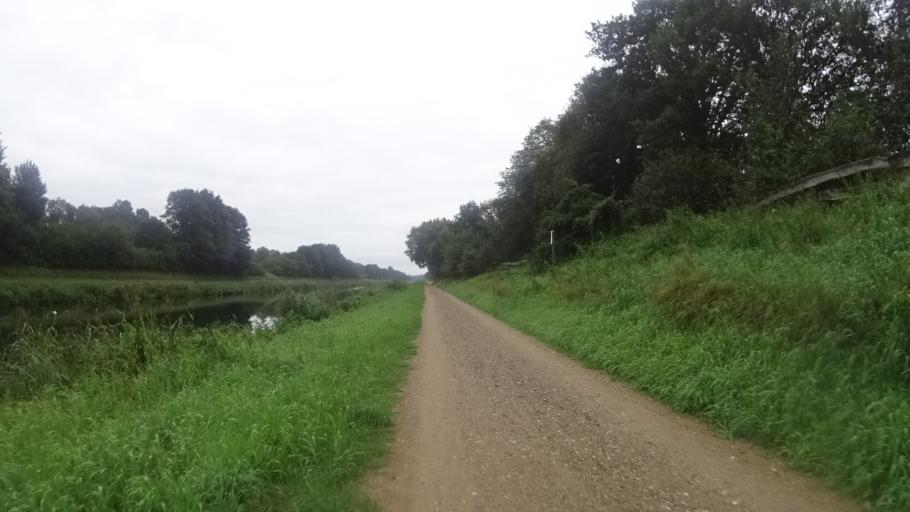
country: DE
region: Schleswig-Holstein
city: Grambek
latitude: 53.5657
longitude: 10.6772
